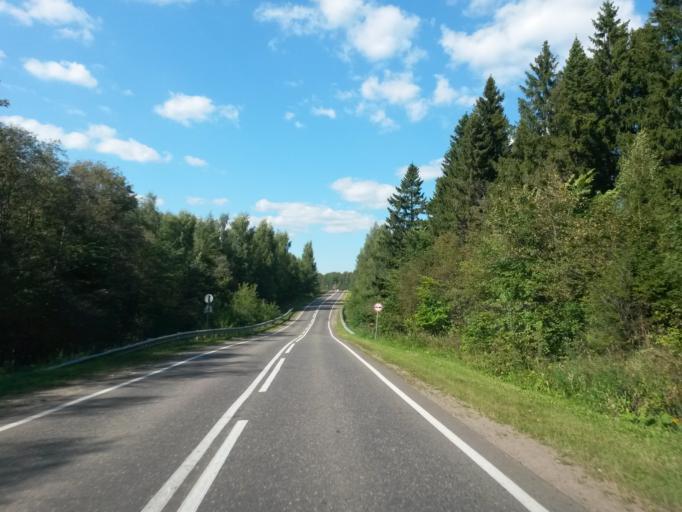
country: RU
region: Jaroslavl
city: Yaroslavl
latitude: 57.7956
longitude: 39.8280
